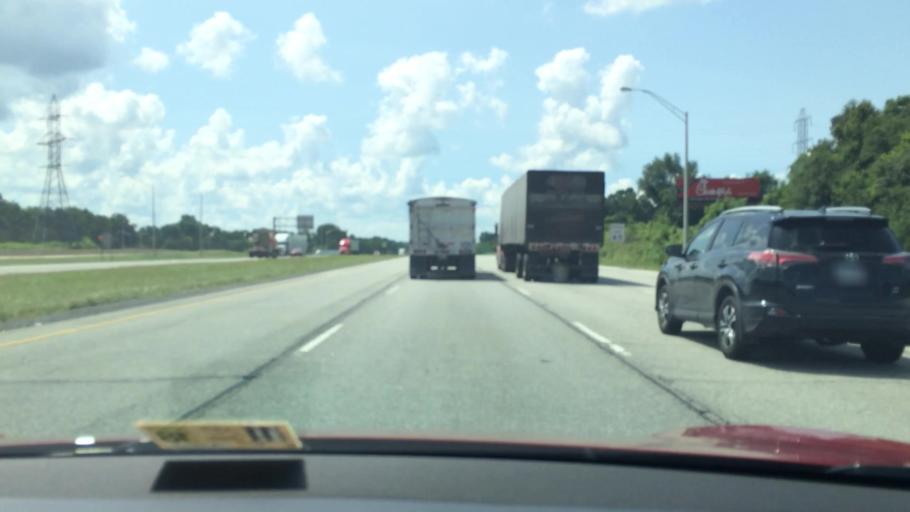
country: US
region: Indiana
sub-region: Saint Joseph County
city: South Bend
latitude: 41.7206
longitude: -86.3394
